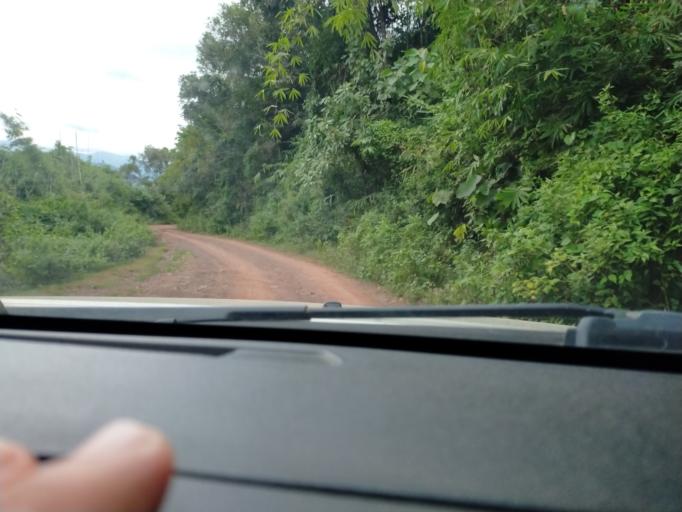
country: TH
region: Nan
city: Chaloem Phra Kiat
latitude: 19.7745
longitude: 101.3484
